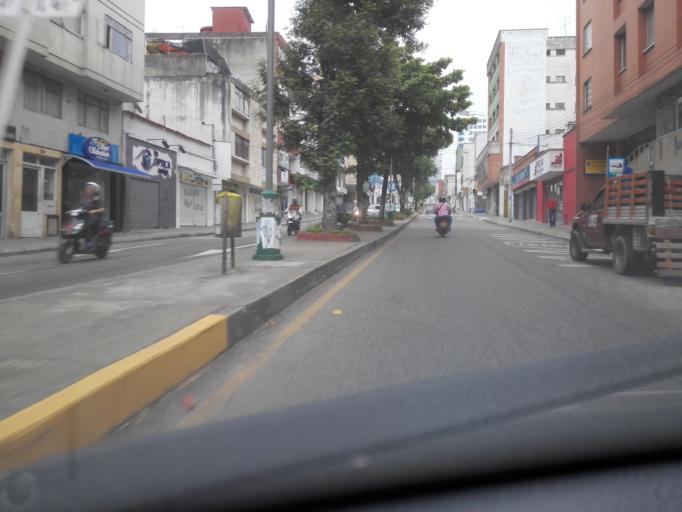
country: CO
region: Santander
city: Bucaramanga
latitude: 7.1199
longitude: -73.1206
